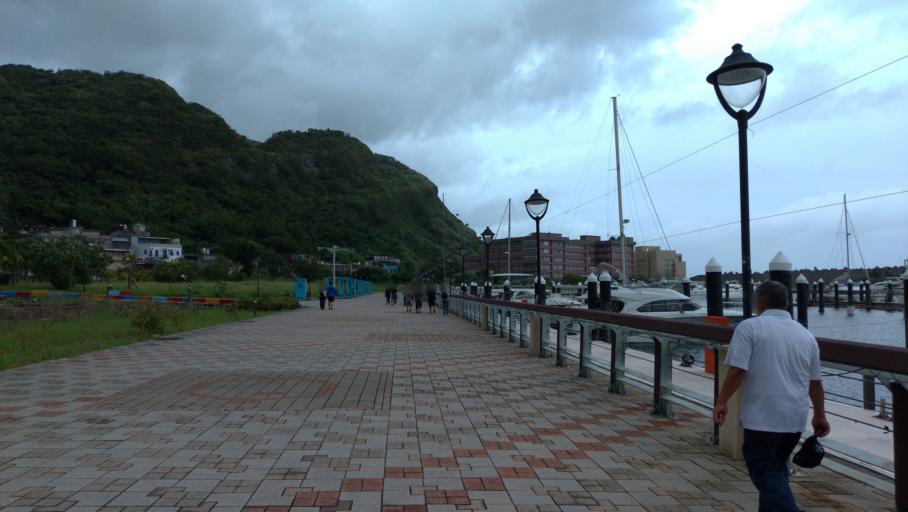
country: TW
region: Taiwan
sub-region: Keelung
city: Keelung
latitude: 25.1462
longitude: 121.7856
